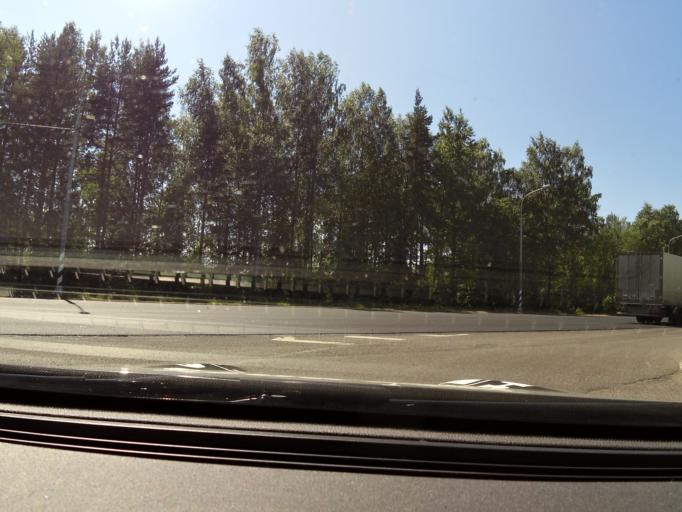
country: RU
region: Novgorod
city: Valday
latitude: 57.9552
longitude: 33.2558
